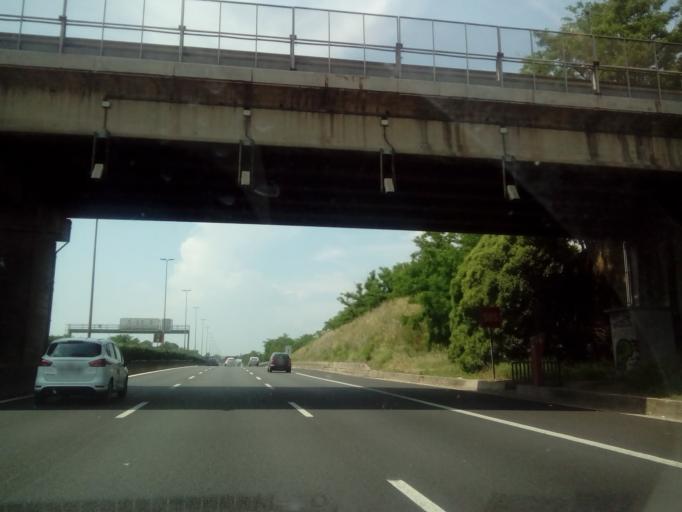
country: IT
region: Latium
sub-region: Citta metropolitana di Roma Capitale
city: Colle Verde
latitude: 41.9627
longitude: 12.5715
